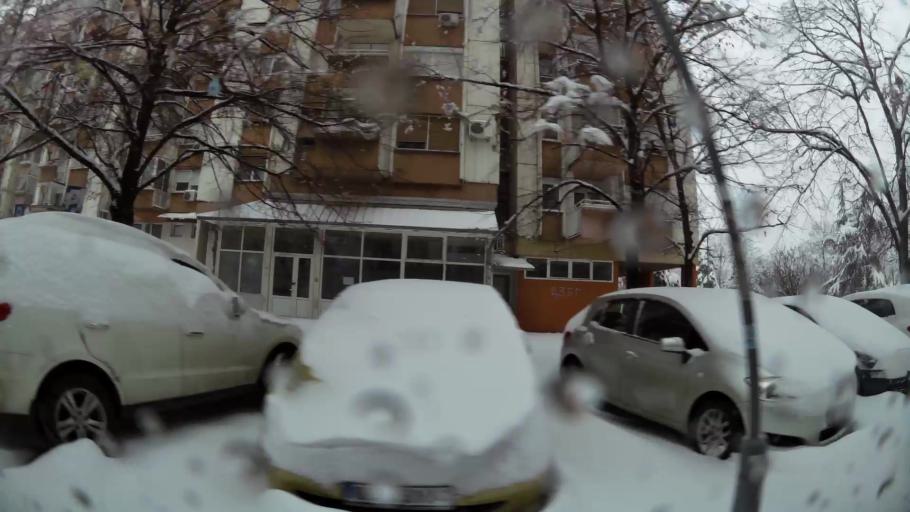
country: RS
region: Central Serbia
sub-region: Belgrade
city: Stari Grad
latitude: 44.8256
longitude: 20.4640
